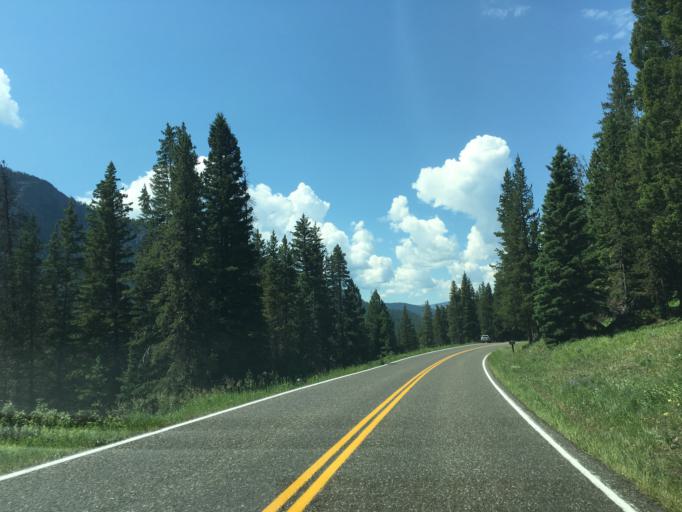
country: US
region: Montana
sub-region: Park County
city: Livingston
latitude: 44.9228
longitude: -110.0941
